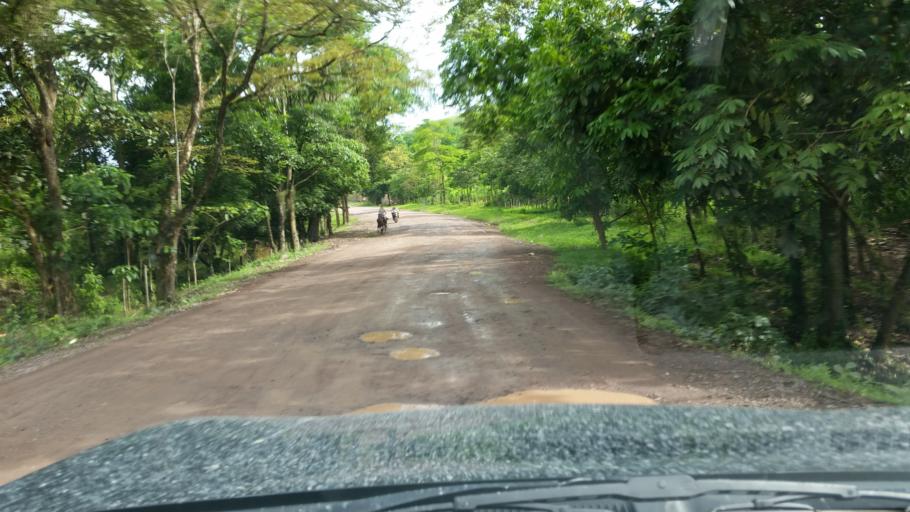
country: NI
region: Atlantico Norte (RAAN)
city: Siuna
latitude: 13.5073
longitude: -84.8440
